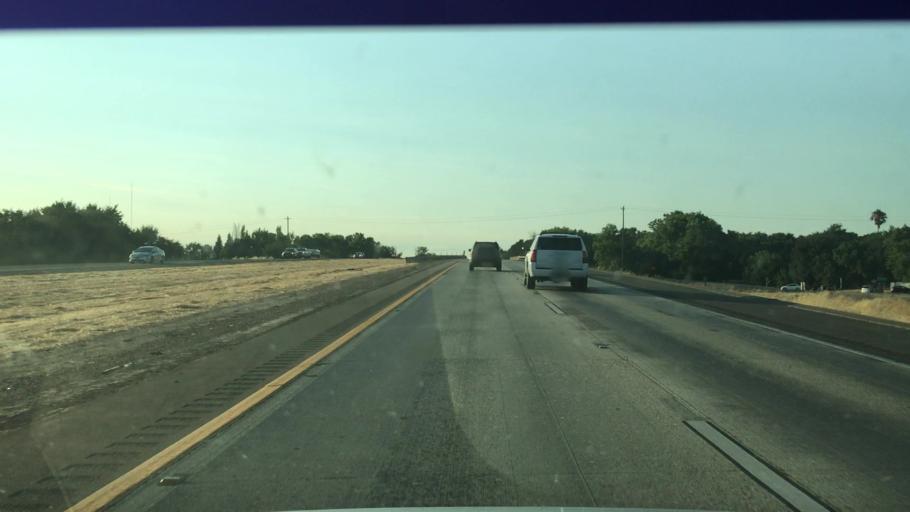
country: US
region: California
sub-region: San Joaquin County
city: Thornton
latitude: 38.2244
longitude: -121.4294
